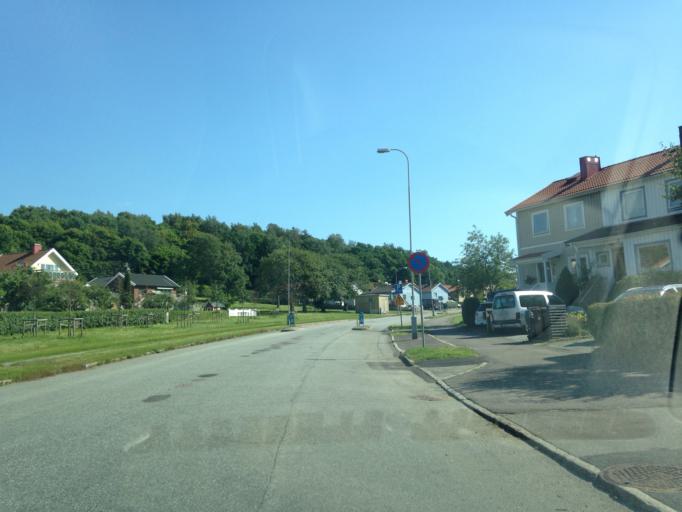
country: SE
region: Vaestra Goetaland
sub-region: Goteborg
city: Majorna
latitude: 57.7293
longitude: 11.9179
